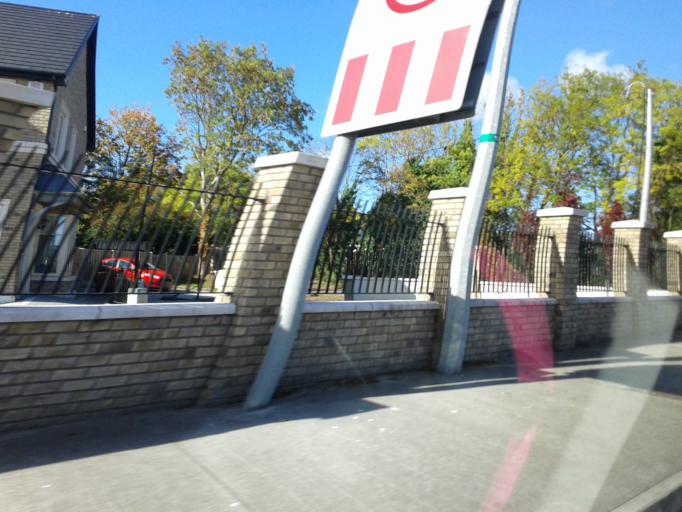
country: IE
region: Leinster
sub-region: An Mhi
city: Ashbourne
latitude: 53.5000
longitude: -6.3876
